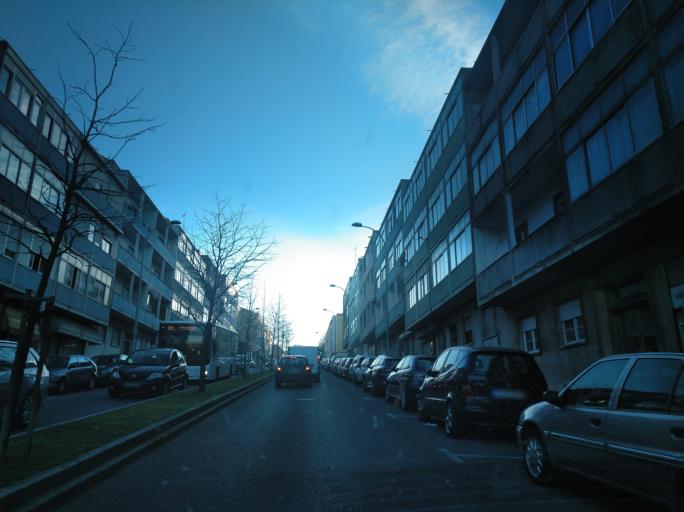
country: PT
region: Lisbon
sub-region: Amadora
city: Amadora
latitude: 38.7468
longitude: -9.2167
